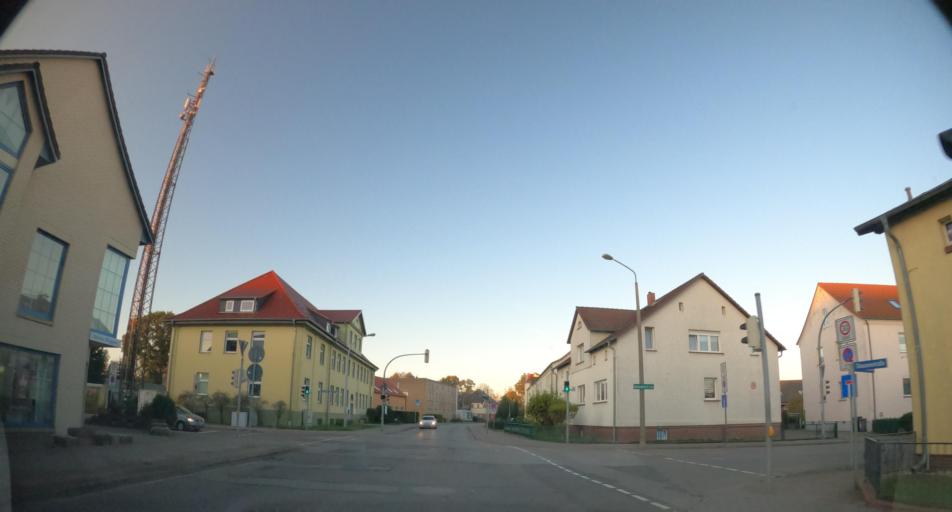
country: DE
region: Mecklenburg-Vorpommern
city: Ueckermunde
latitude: 53.7359
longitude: 14.0392
